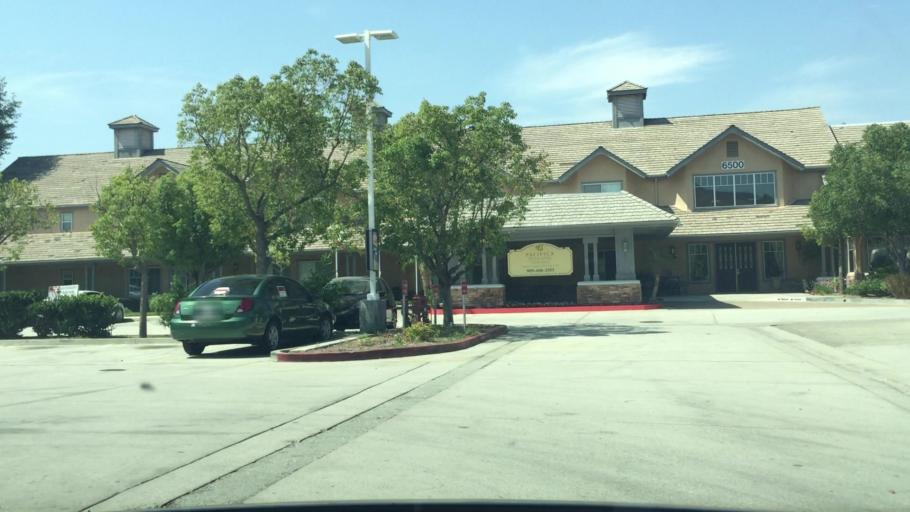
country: US
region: California
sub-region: San Bernardino County
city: Los Serranos
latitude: 33.9305
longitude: -117.6627
